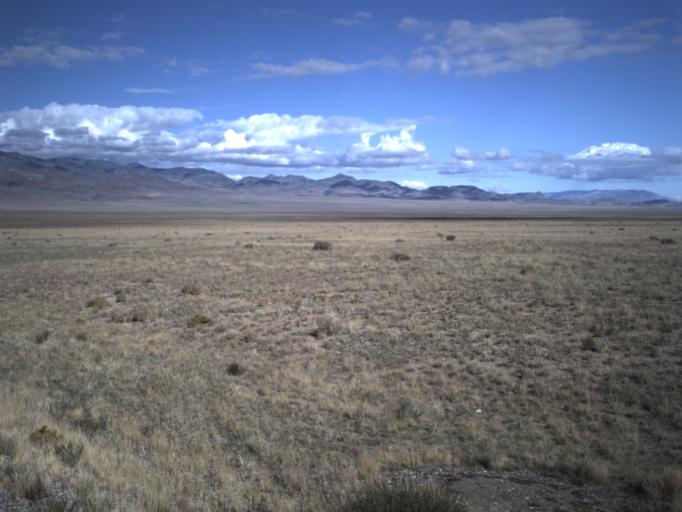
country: US
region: Utah
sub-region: Beaver County
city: Milford
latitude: 38.4539
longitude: -113.3559
